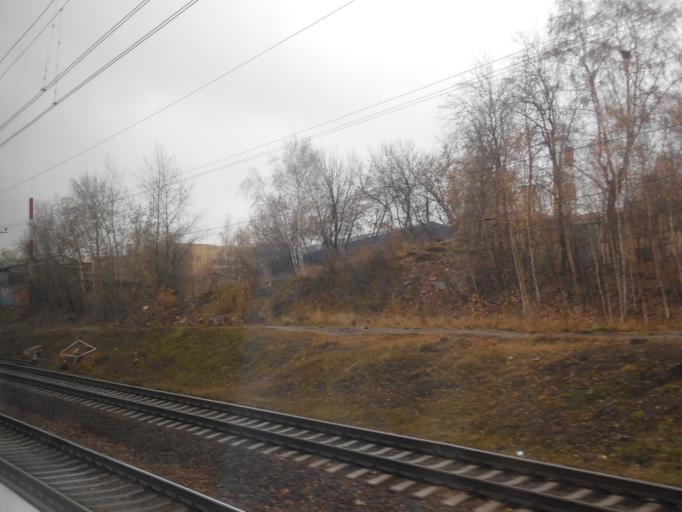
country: RU
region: Moscow
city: Kotlovka
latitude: 55.6792
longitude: 37.6215
